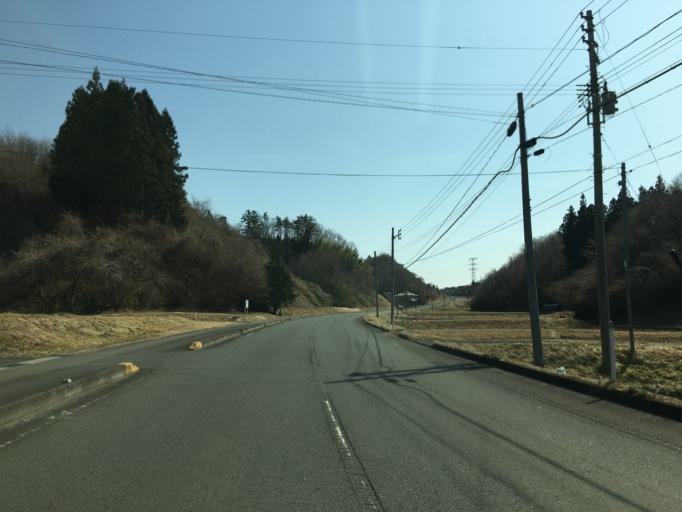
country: JP
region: Fukushima
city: Ishikawa
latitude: 37.0435
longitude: 140.4696
